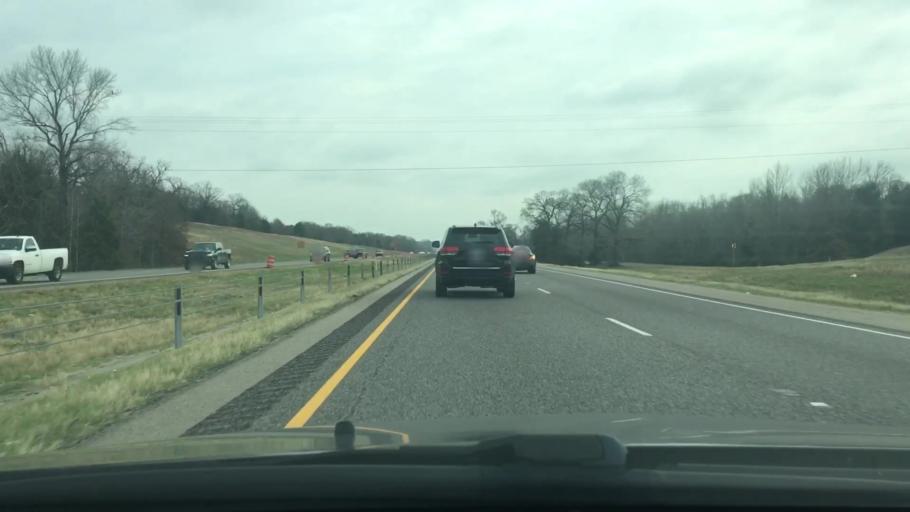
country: US
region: Texas
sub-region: Leon County
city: Buffalo
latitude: 31.4987
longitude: -96.0969
